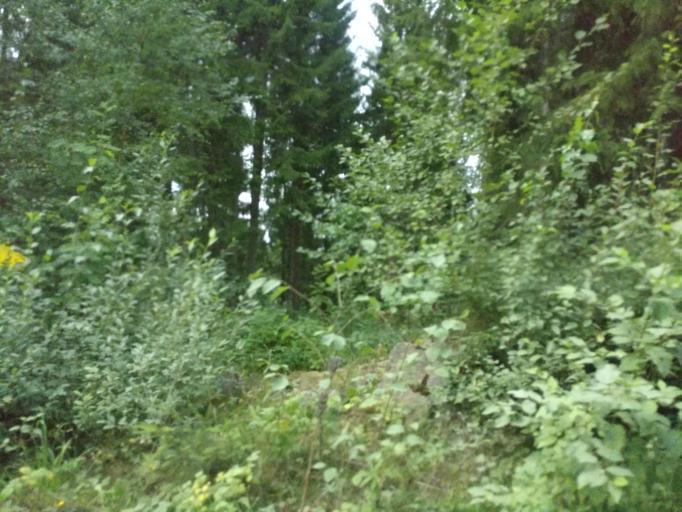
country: SE
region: Vaermland
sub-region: Hagfors Kommun
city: Hagfors
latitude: 60.0144
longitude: 13.6938
